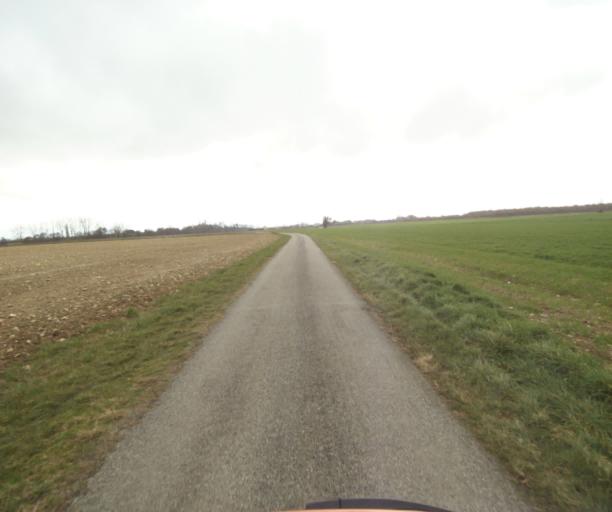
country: FR
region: Languedoc-Roussillon
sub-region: Departement de l'Aude
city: Belpech
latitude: 43.1775
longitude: 1.6929
